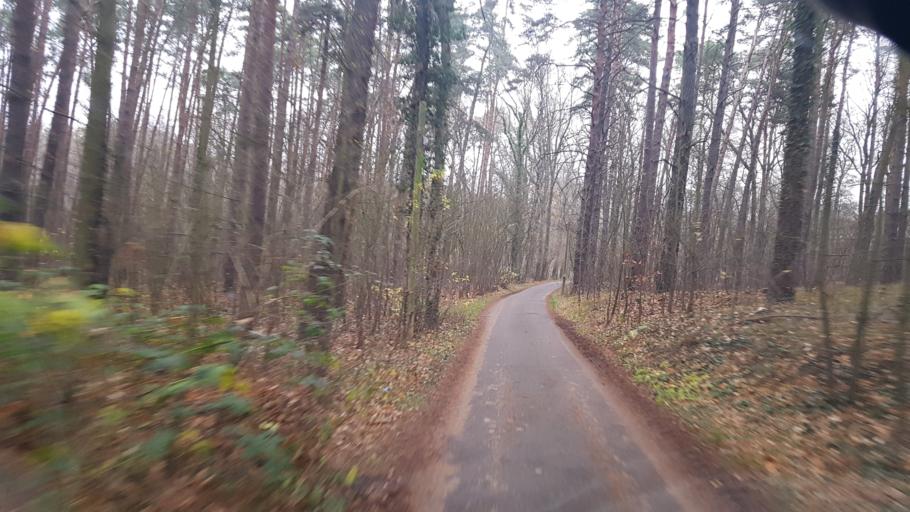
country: DE
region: Brandenburg
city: Schenkendobern
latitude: 51.9710
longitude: 14.6497
